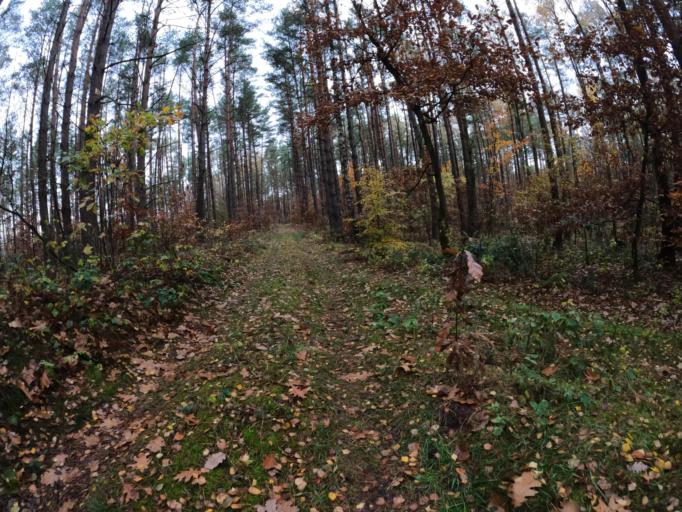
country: PL
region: West Pomeranian Voivodeship
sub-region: Powiat walecki
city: Tuczno
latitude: 53.2796
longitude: 16.2463
